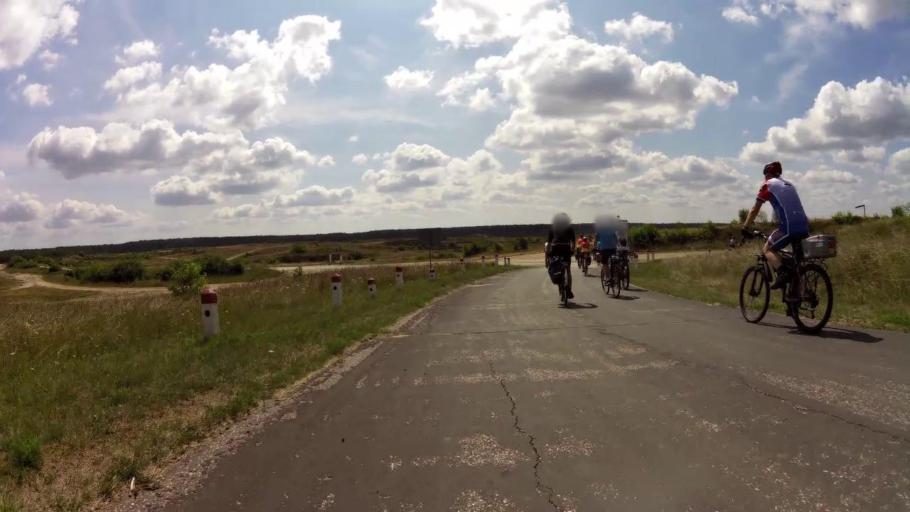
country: PL
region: West Pomeranian Voivodeship
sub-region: Powiat drawski
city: Drawsko Pomorskie
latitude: 53.4513
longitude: 15.7753
